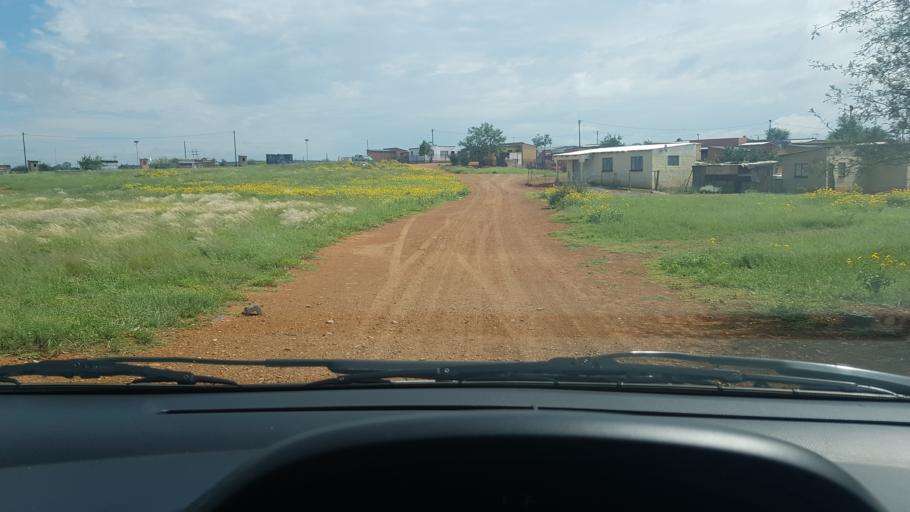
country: ZA
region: Northern Cape
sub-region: Siyanda District Municipality
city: Danielskuil
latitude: -28.1980
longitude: 23.5538
